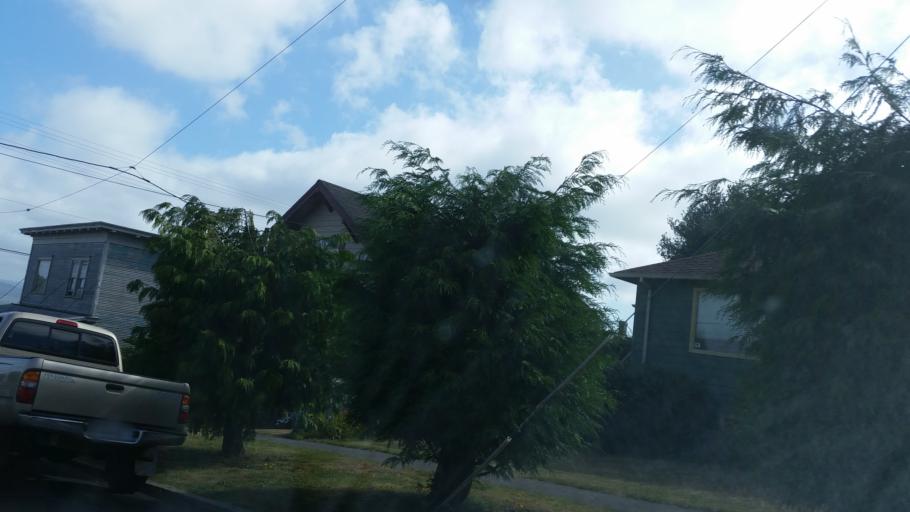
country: US
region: Oregon
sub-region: Clatsop County
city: Astoria
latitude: 46.1930
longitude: -123.8015
